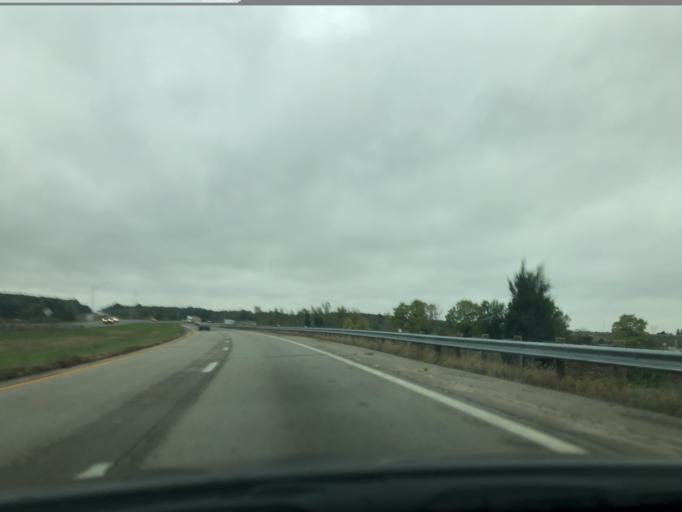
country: US
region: Ohio
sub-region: Union County
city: Marysville
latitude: 40.2435
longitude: -83.3982
